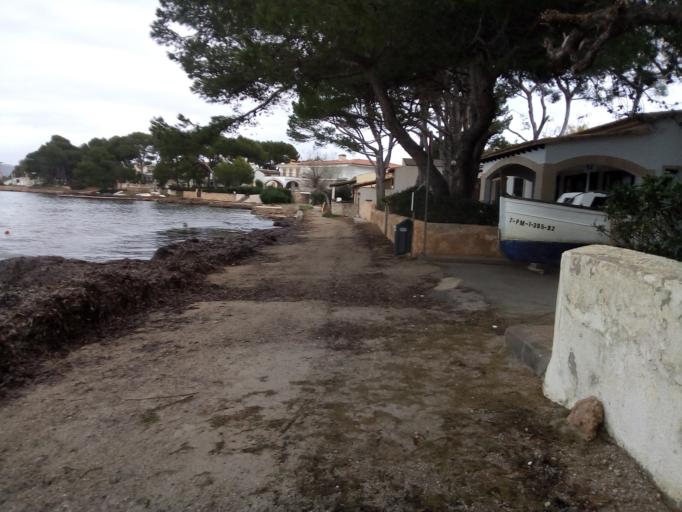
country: ES
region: Balearic Islands
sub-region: Illes Balears
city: Alcudia
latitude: 39.8615
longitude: 3.1147
